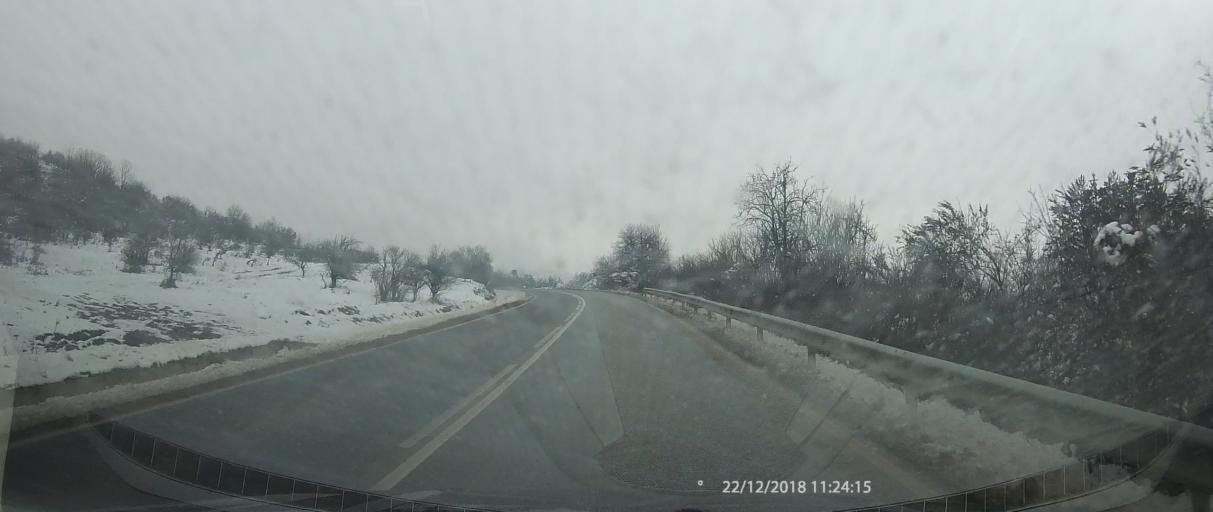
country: BG
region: Kyustendil
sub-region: Obshtina Boboshevo
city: Boboshevo
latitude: 42.2503
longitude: 22.8890
